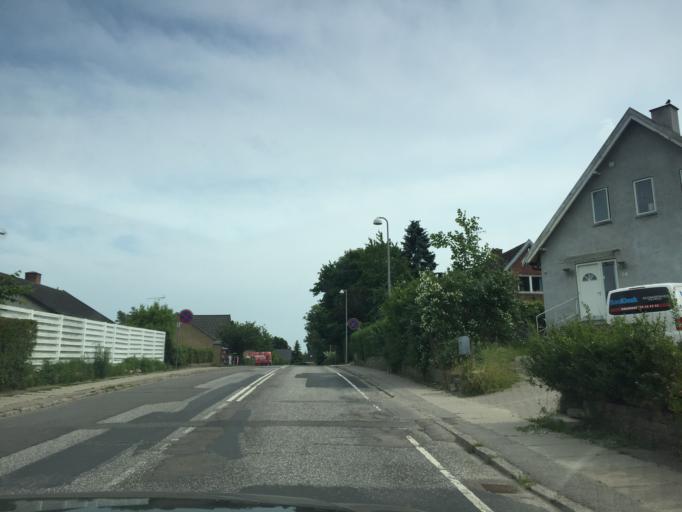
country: DK
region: Capital Region
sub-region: Hoje-Taastrup Kommune
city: Flong
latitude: 55.6553
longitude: 12.1883
